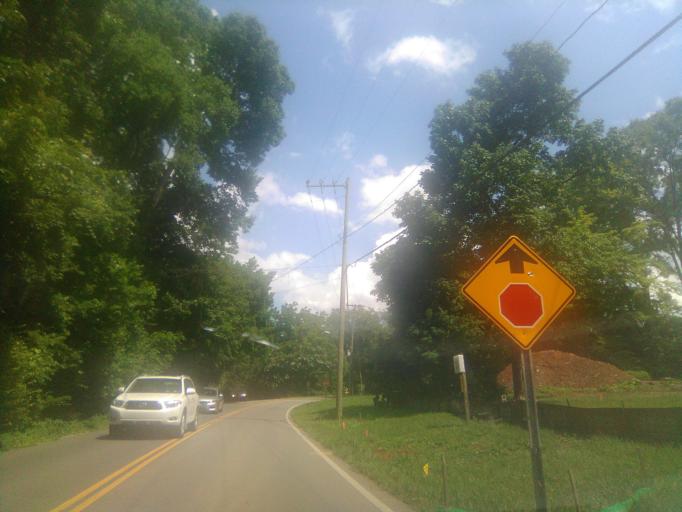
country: US
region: Tennessee
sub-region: Davidson County
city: Belle Meade
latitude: 36.1110
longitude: -86.8456
